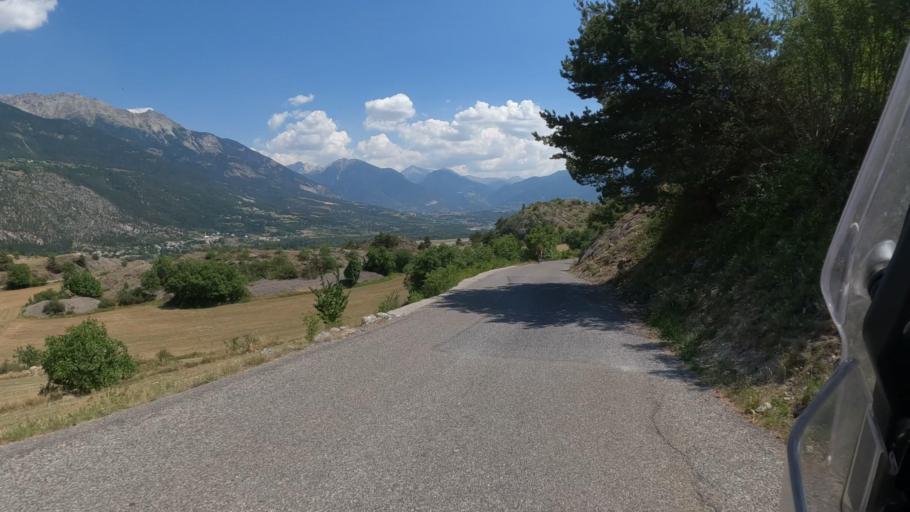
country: FR
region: Provence-Alpes-Cote d'Azur
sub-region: Departement des Hautes-Alpes
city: Guillestre
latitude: 44.7116
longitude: 6.5849
